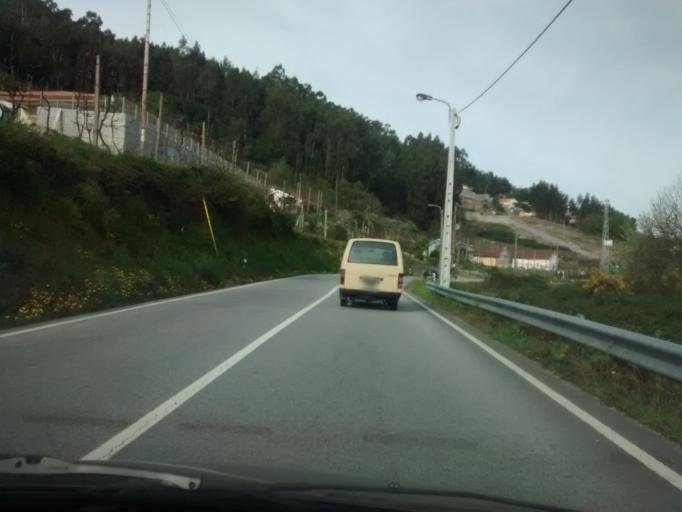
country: PT
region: Braga
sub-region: Braga
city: Braga
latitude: 41.5022
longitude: -8.3950
